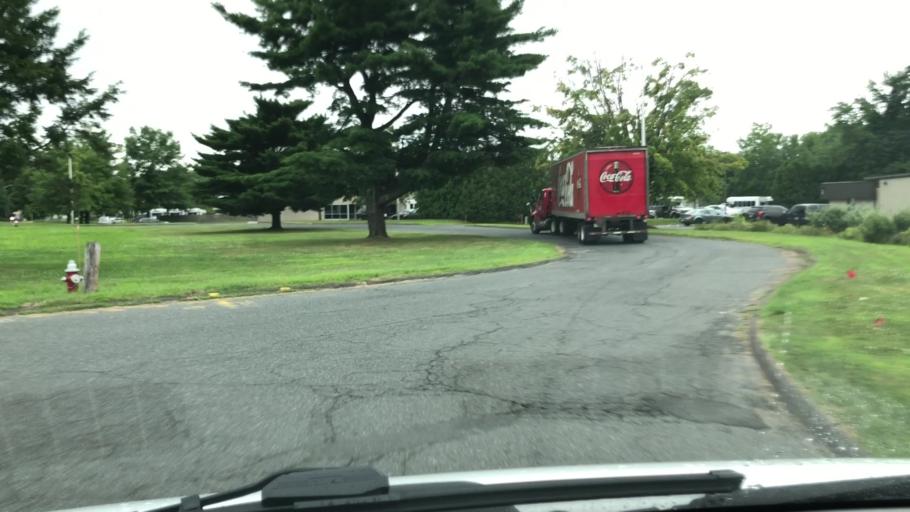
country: US
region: Massachusetts
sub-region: Hampshire County
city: Northampton
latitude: 42.3345
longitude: -72.6302
